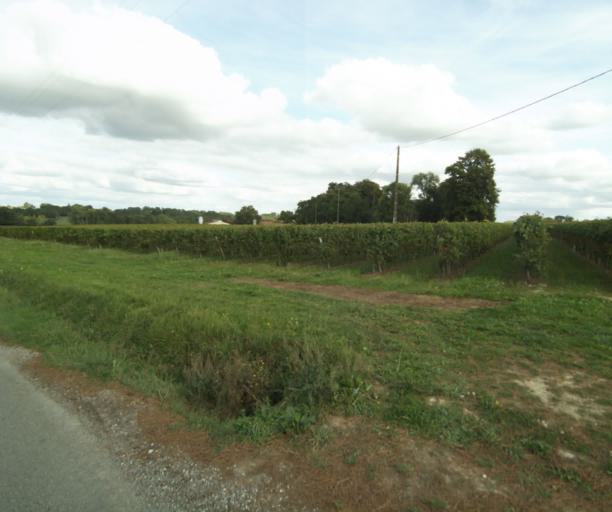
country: FR
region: Midi-Pyrenees
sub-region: Departement du Gers
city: Eauze
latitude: 43.8558
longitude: 0.1630
